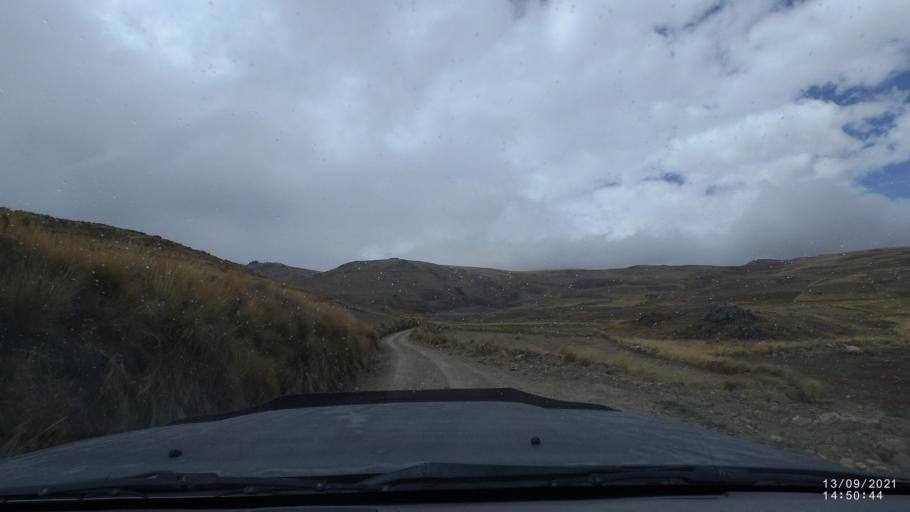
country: BO
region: Cochabamba
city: Colomi
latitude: -17.3465
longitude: -65.7935
